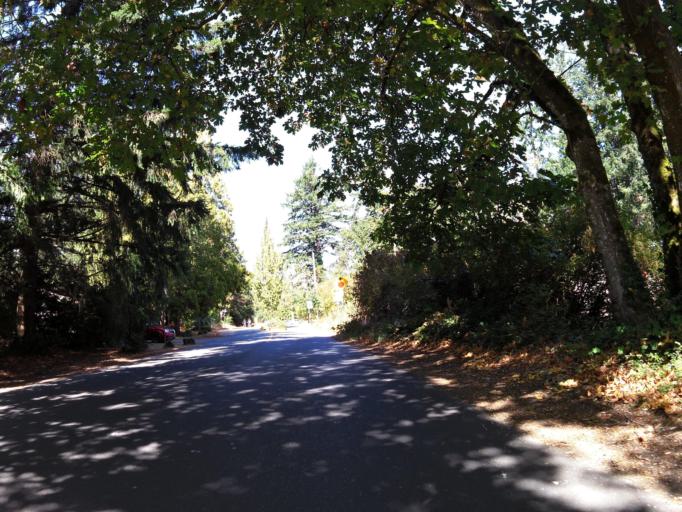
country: CA
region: British Columbia
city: Victoria
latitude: 48.5280
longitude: -123.3728
